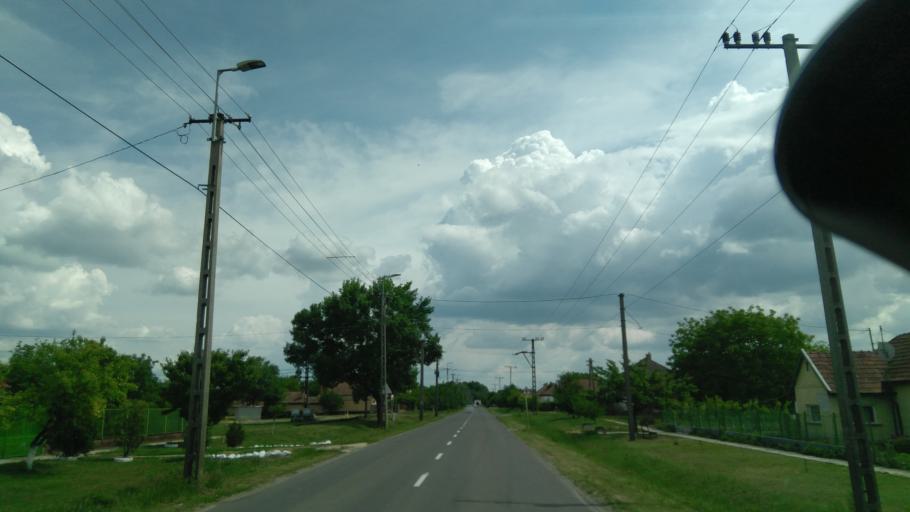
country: HU
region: Bekes
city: Mezohegyes
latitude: 46.3261
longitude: 20.8127
